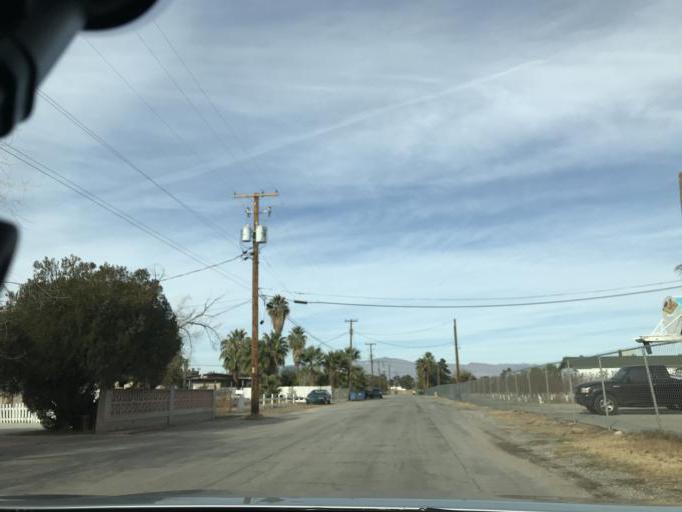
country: US
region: Nevada
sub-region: Clark County
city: Las Vegas
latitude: 36.1781
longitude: -115.1670
